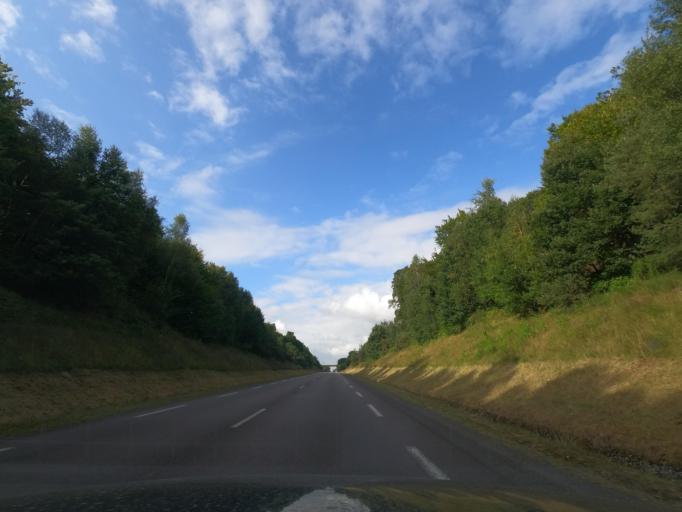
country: FR
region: Haute-Normandie
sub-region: Departement de l'Eure
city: Bernay
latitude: 49.0882
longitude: 0.5745
